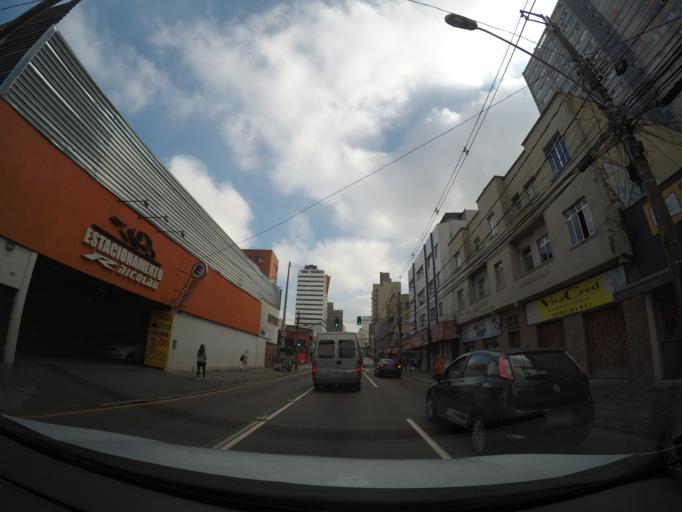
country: BR
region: Parana
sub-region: Curitiba
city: Curitiba
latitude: -25.4332
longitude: -49.2636
